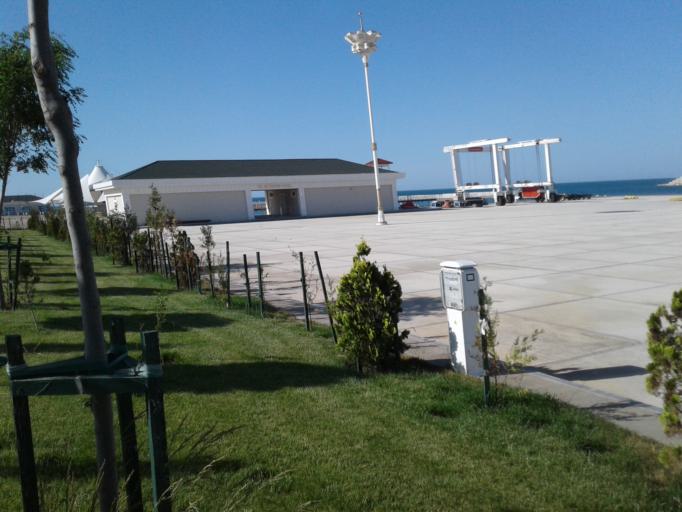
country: TM
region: Balkan
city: Turkmenbasy
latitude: 39.9843
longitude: 52.8202
